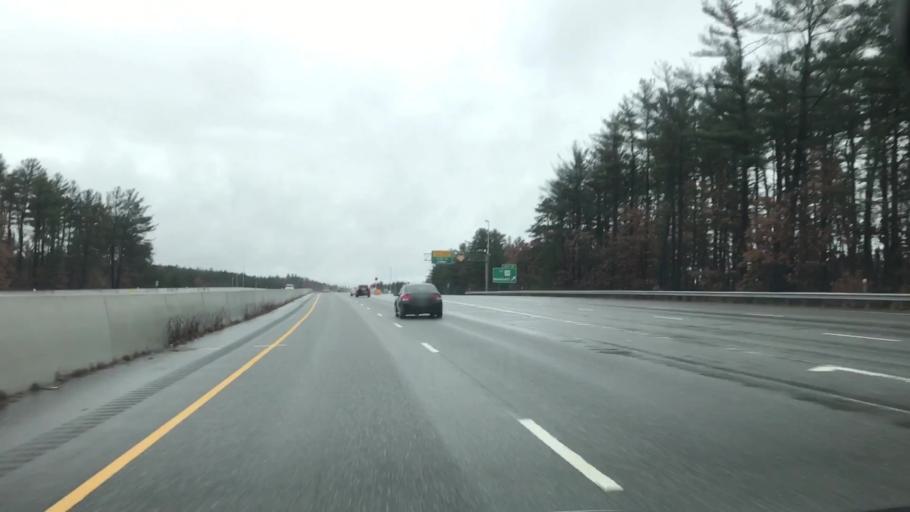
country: US
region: New Hampshire
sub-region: Merrimack County
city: Hooksett
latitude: 43.0795
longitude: -71.4724
